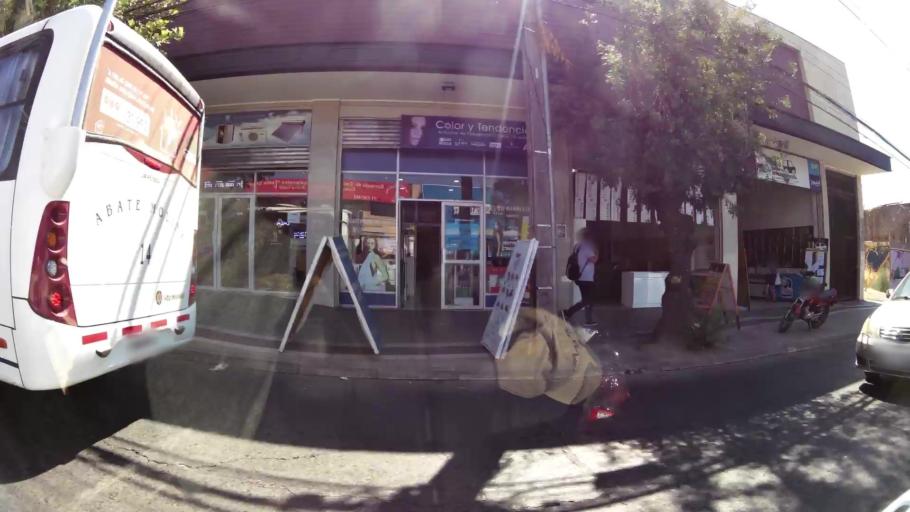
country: CL
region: Maule
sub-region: Provincia de Talca
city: Talca
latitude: -35.4271
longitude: -71.6502
